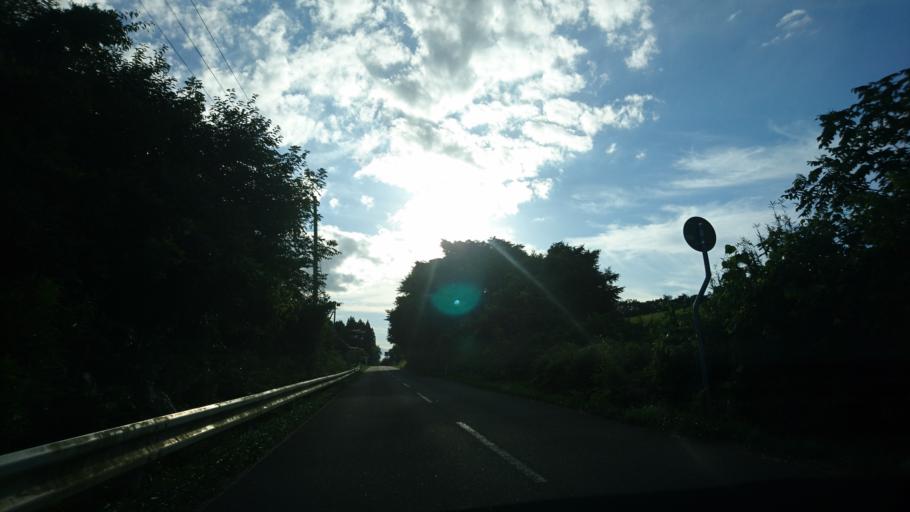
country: JP
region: Iwate
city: Ichinoseki
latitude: 38.8349
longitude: 141.1074
